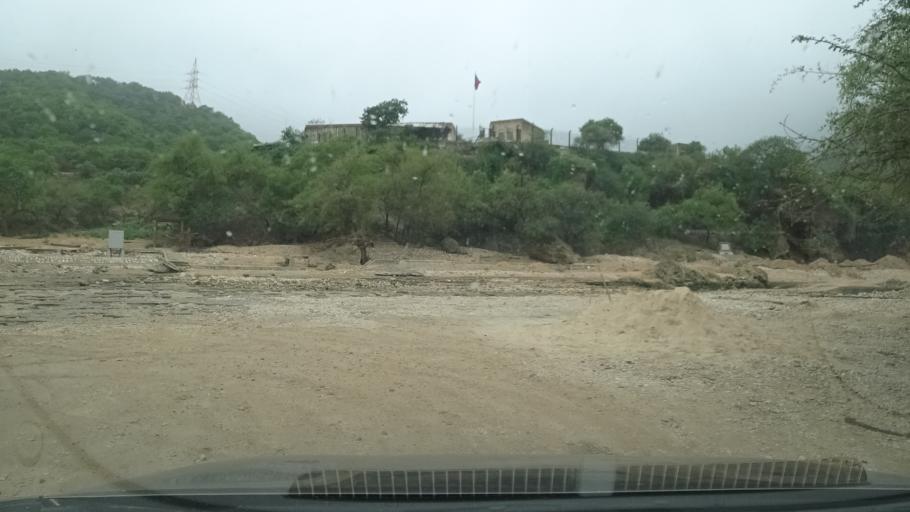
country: OM
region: Zufar
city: Salalah
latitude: 17.1056
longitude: 54.0750
